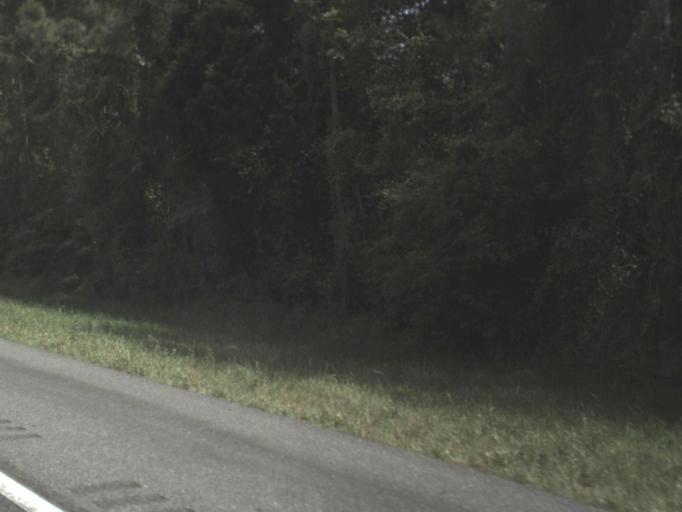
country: US
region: Florida
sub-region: Suwannee County
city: Live Oak
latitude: 30.3428
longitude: -83.1303
